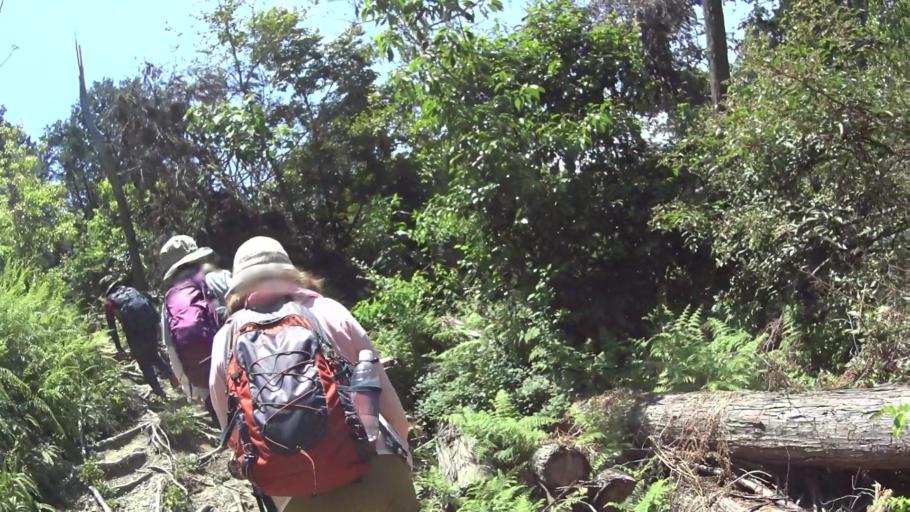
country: JP
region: Kyoto
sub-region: Kyoto-shi
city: Kamigyo-ku
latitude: 35.0112
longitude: 135.8042
